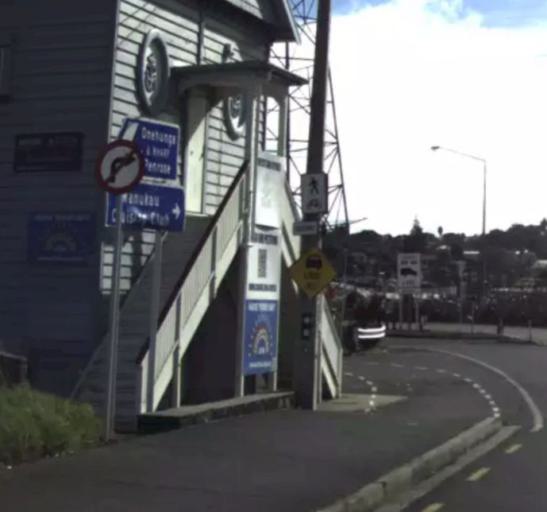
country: NZ
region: Auckland
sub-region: Auckland
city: Mangere
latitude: -36.9300
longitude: 174.7822
